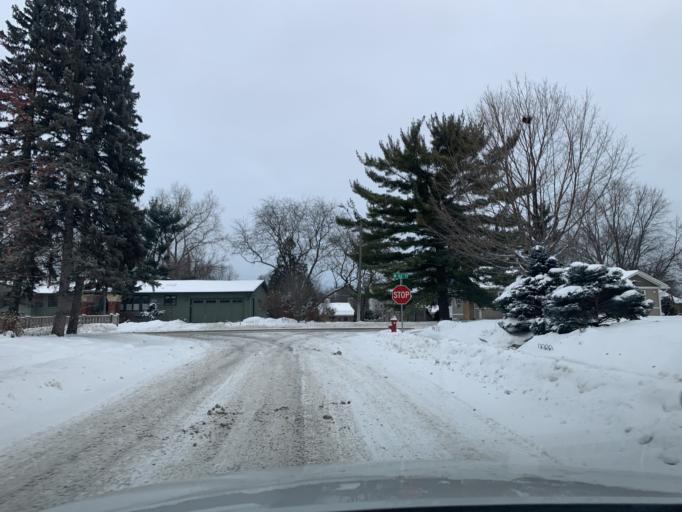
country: US
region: Minnesota
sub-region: Hennepin County
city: Saint Louis Park
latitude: 44.9191
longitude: -93.3472
